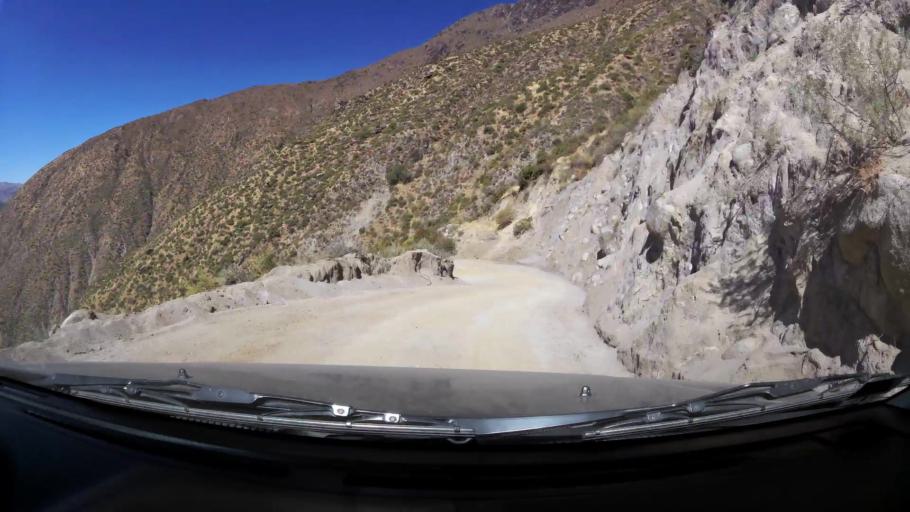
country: PE
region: Huancavelica
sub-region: Huaytara
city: Quito-Arma
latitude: -13.6180
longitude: -75.3500
